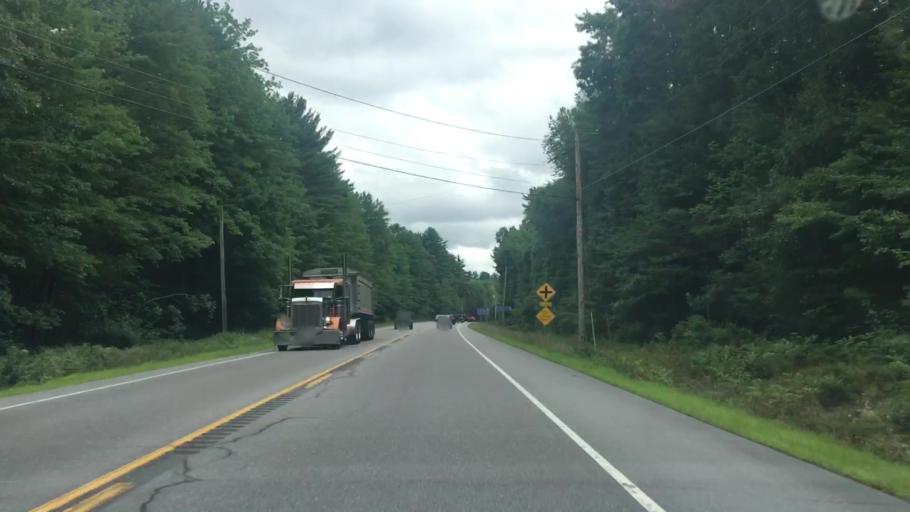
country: US
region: Maine
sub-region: York County
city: Waterboro
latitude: 43.5143
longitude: -70.7180
